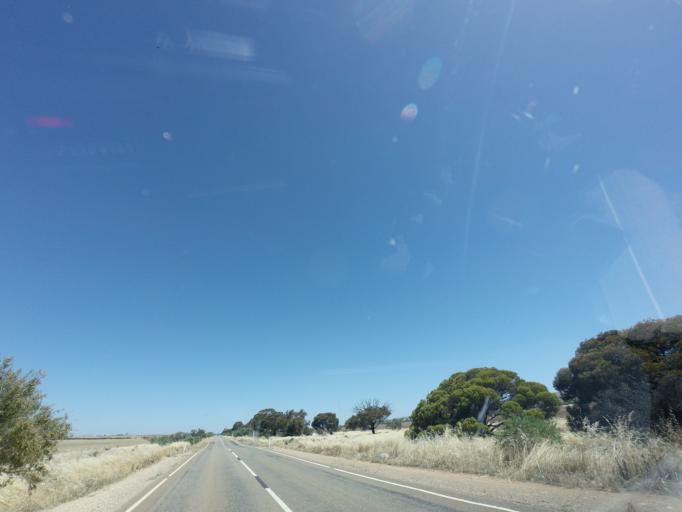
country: AU
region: South Australia
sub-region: Peterborough
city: Peterborough
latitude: -32.7758
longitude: 138.6639
